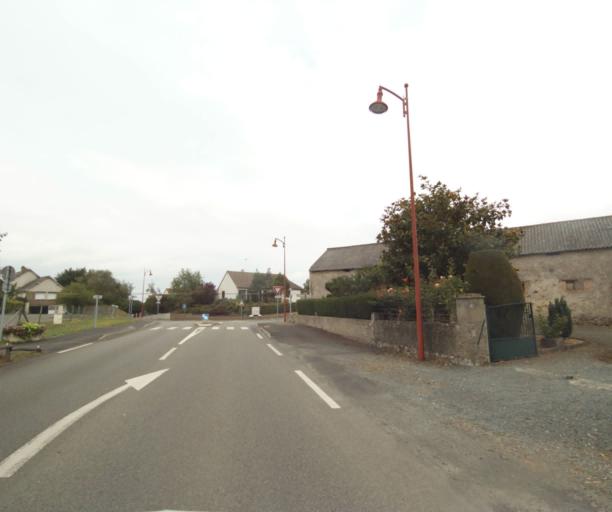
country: FR
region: Pays de la Loire
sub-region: Departement de la Sarthe
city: Solesmes
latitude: 47.8454
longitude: -0.2977
